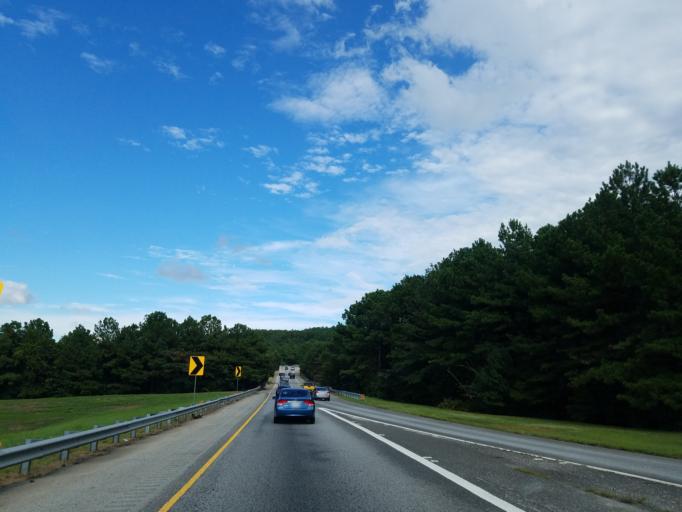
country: US
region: Georgia
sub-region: Clayton County
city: Conley
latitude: 33.6698
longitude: -84.3315
